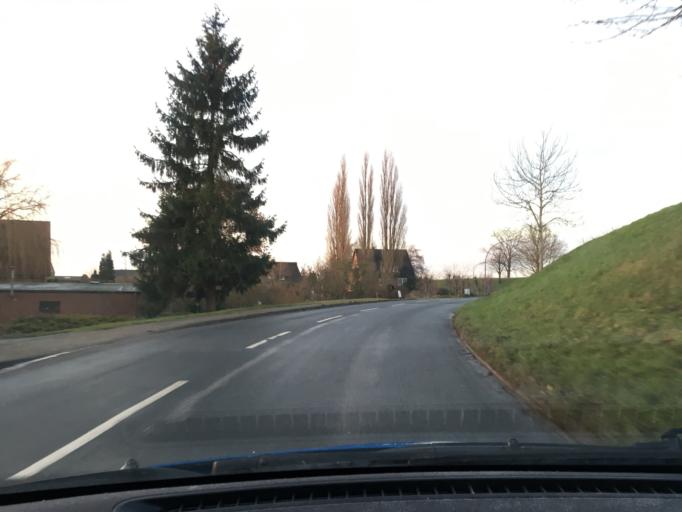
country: DE
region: Lower Saxony
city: Neu Wulmstorf
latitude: 53.5092
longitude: 9.8330
